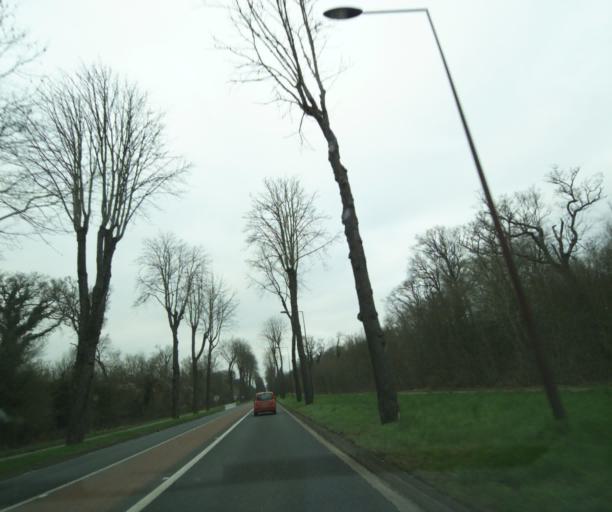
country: FR
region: Ile-de-France
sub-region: Departement des Yvelines
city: Poissy
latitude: 48.9160
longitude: 2.0657
